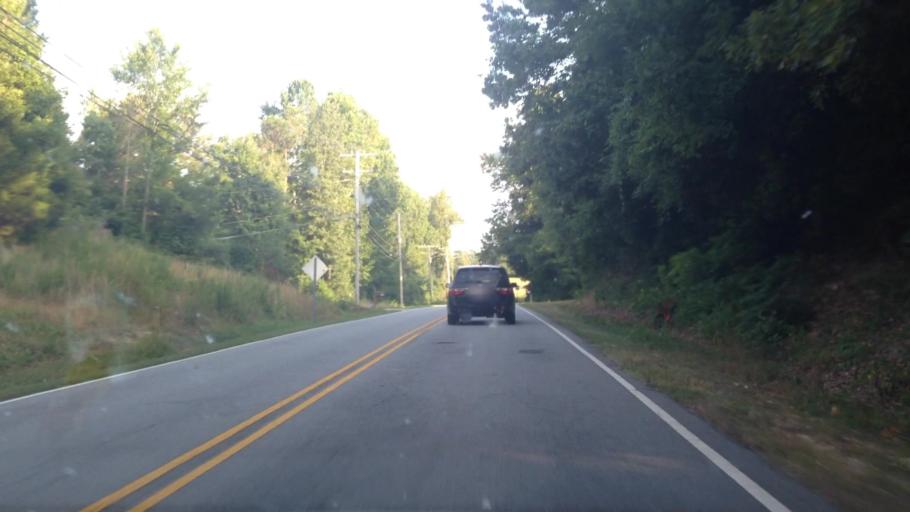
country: US
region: North Carolina
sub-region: Davidson County
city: Thomasville
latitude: 35.9454
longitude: -80.0754
